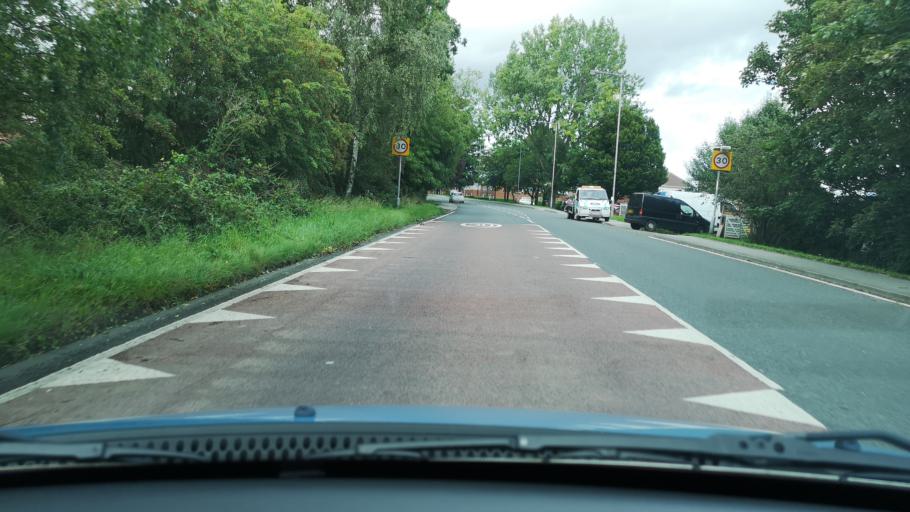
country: GB
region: England
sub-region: City and Borough of Wakefield
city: Low Ackworth
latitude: 53.6393
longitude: -1.3303
